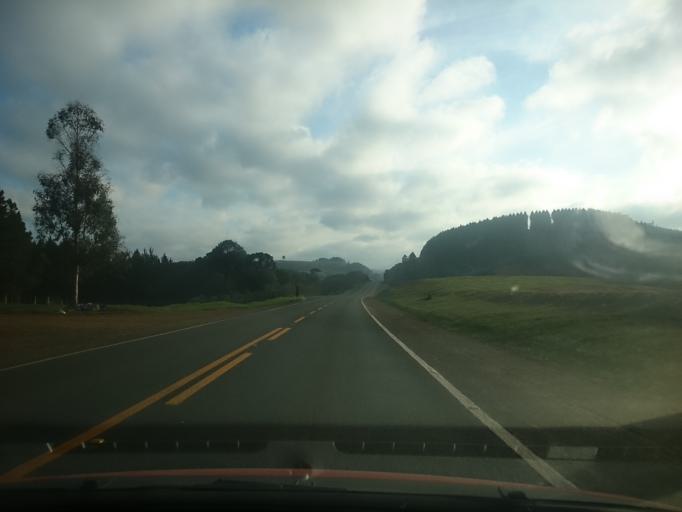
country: BR
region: Santa Catarina
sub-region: Lages
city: Lages
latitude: -28.0392
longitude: -50.5668
